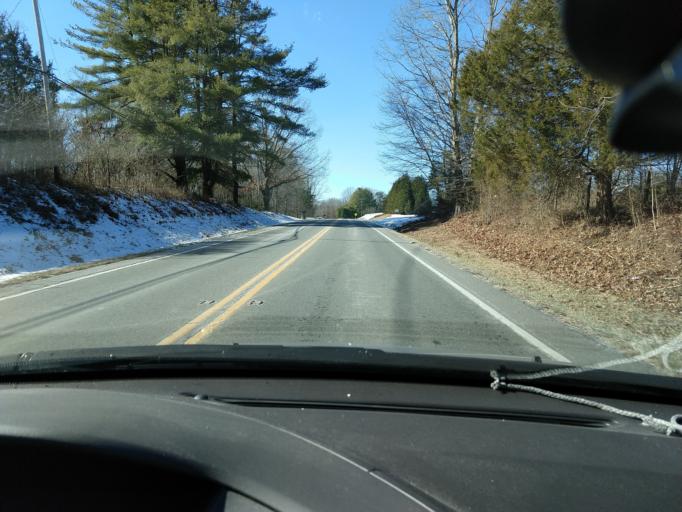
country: US
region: Virginia
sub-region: Franklin County
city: North Shore
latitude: 37.1177
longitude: -79.7963
